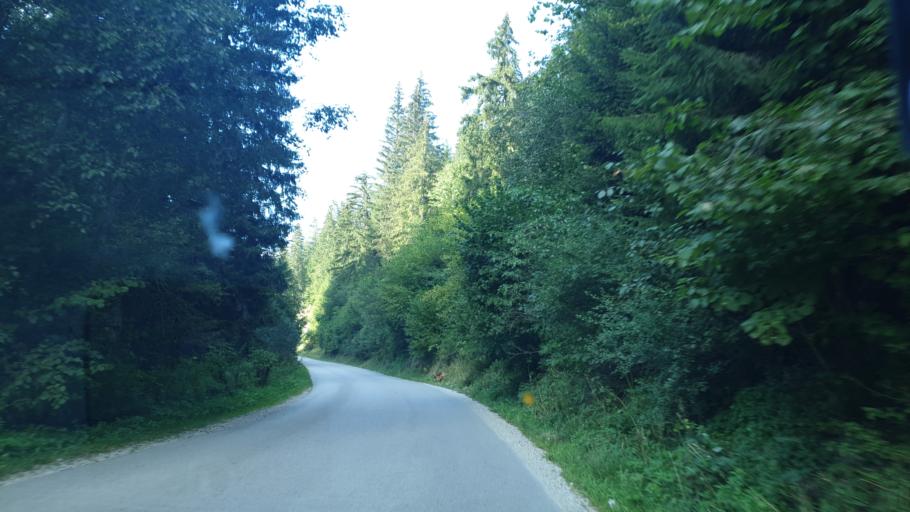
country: RS
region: Central Serbia
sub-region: Zlatiborski Okrug
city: Nova Varos
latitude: 43.4450
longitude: 19.8506
